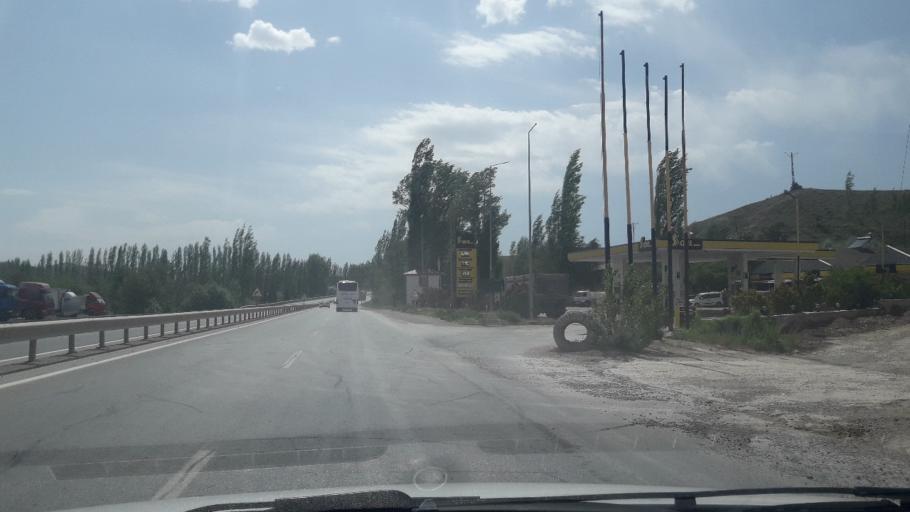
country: TR
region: Sivas
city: Direkli
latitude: 39.7182
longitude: 36.8304
